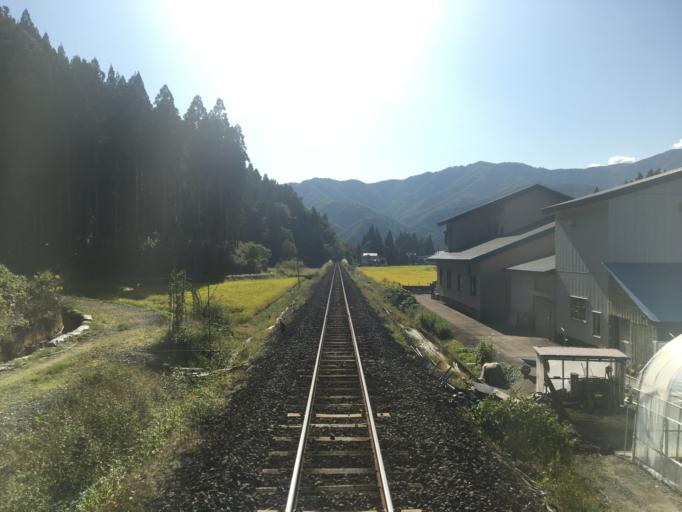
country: JP
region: Akita
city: Kakunodatemachi
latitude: 39.7309
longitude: 140.5734
